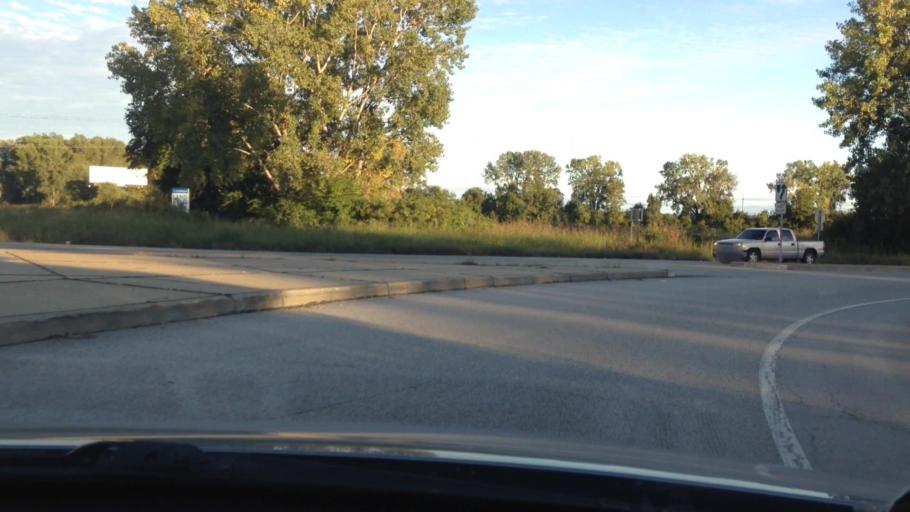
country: US
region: Missouri
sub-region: Clay County
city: Claycomo
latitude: 39.1547
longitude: -94.4775
